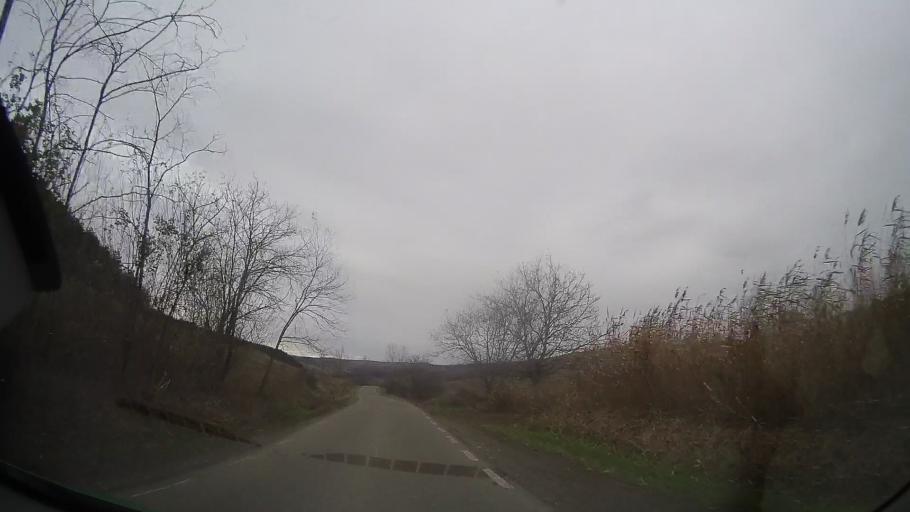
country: RO
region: Mures
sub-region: Comuna Bala
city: Bala
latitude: 46.7138
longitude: 24.5143
